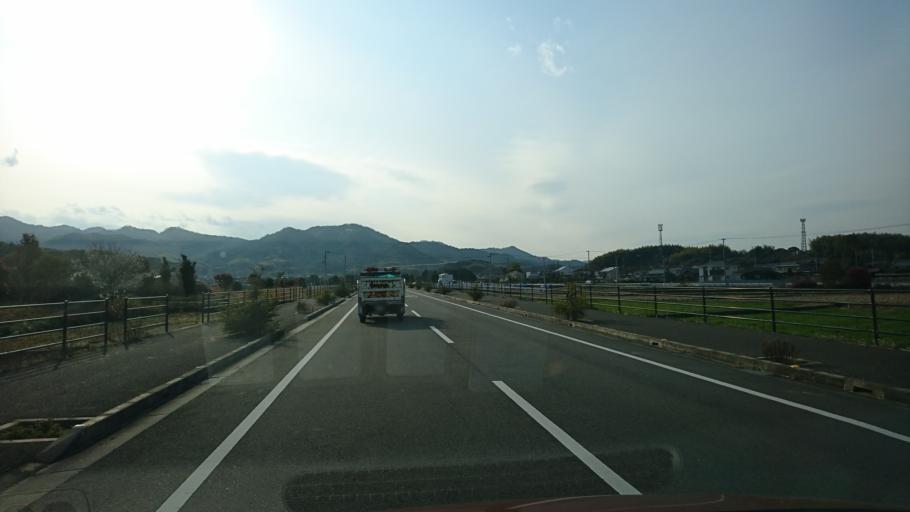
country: JP
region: Ehime
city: Saijo
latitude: 34.0243
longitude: 132.9992
